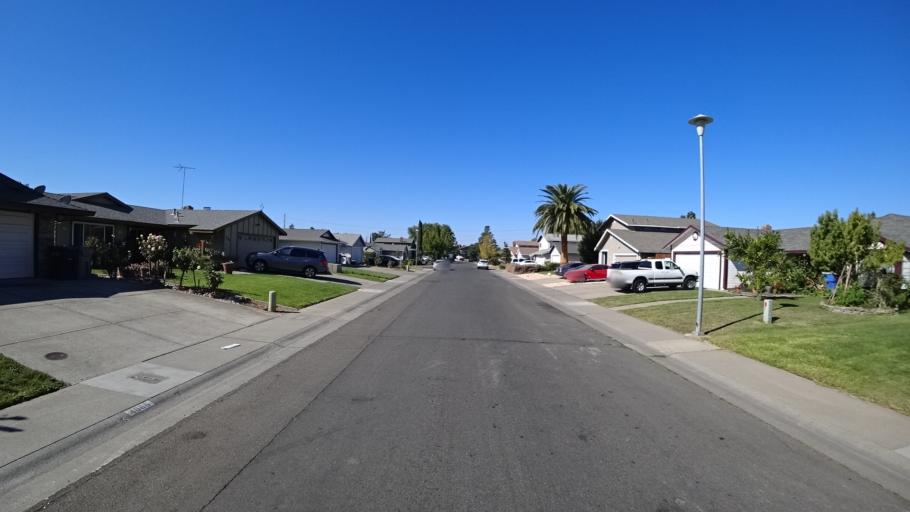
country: US
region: California
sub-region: Sacramento County
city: Parkway
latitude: 38.4708
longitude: -121.4585
